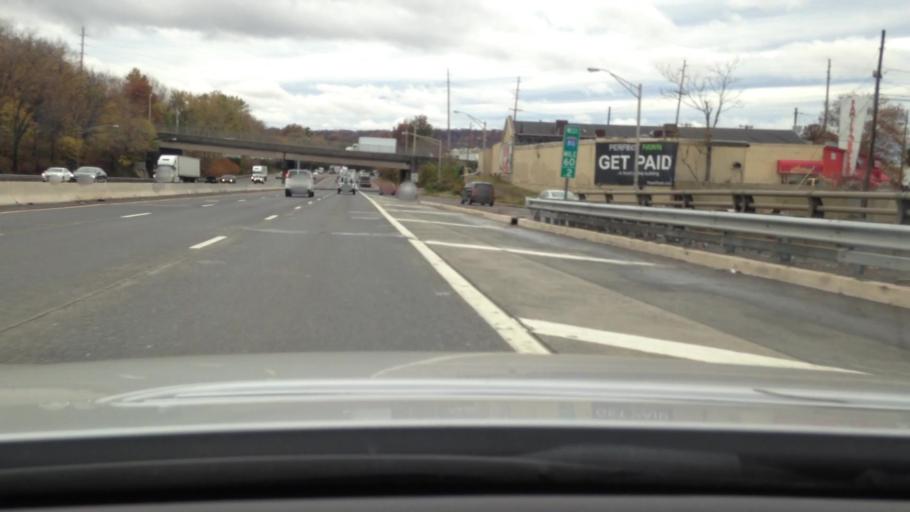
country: US
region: New Jersey
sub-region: Bergen County
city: Elmwood Park
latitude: 40.9016
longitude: -74.1391
